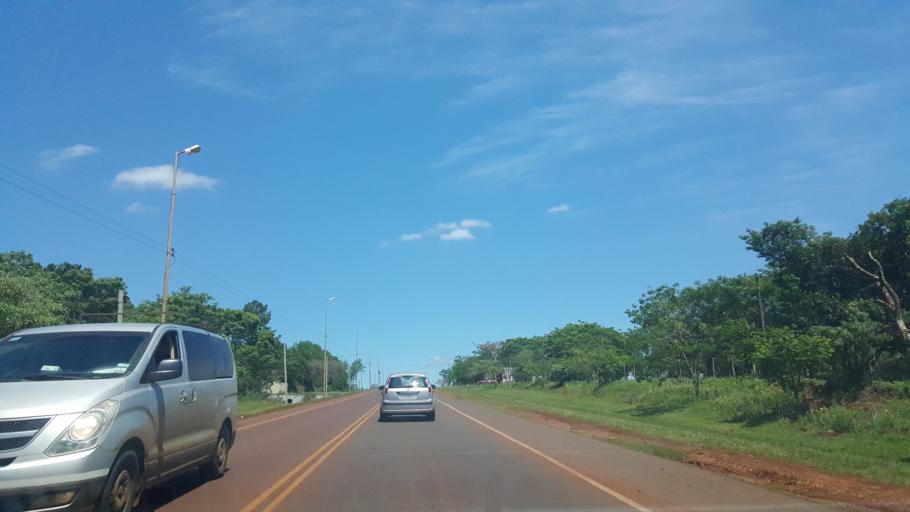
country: AR
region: Misiones
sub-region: Departamento de Capital
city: Posadas
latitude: -27.4035
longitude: -55.9690
